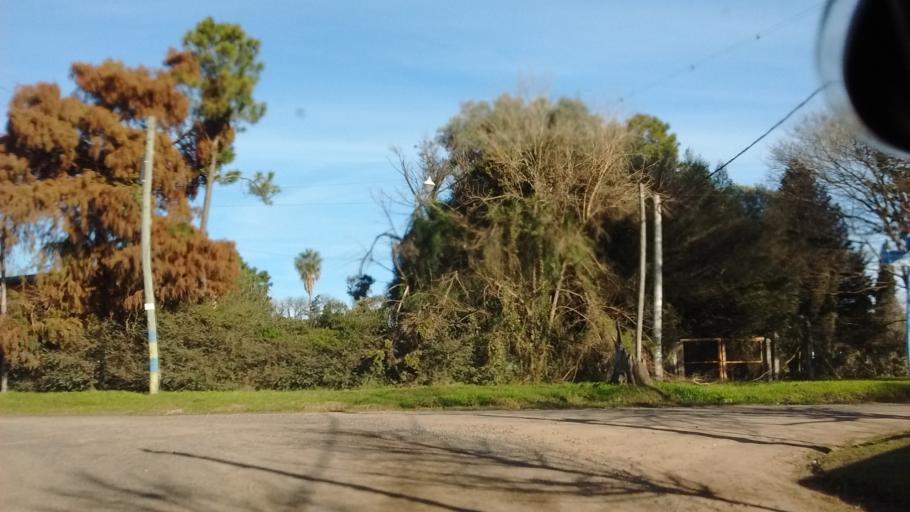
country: AR
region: Santa Fe
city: Funes
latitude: -32.9107
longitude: -60.8131
